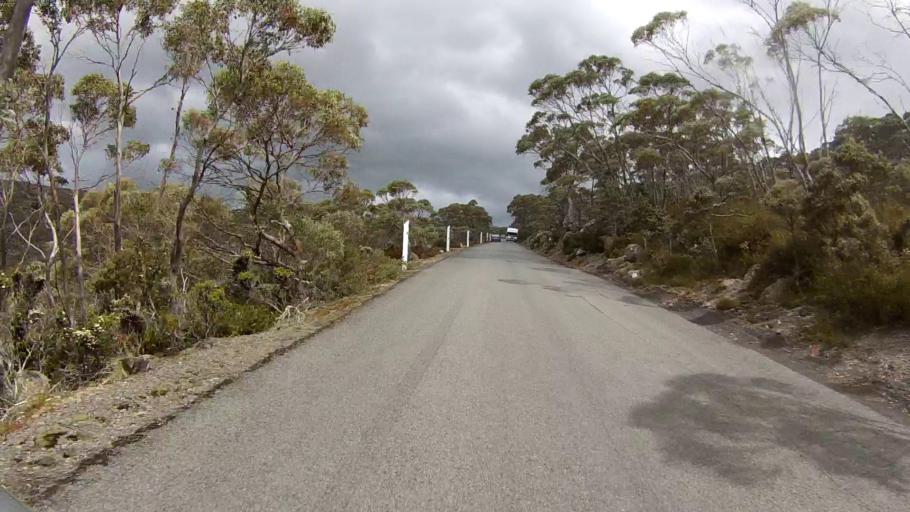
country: AU
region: Tasmania
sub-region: Glenorchy
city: West Moonah
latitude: -42.8869
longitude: 147.2209
